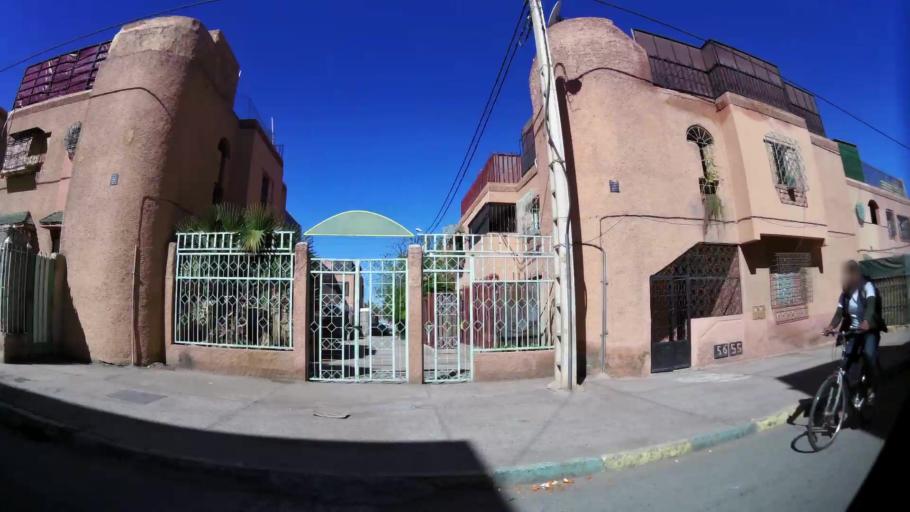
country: MA
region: Marrakech-Tensift-Al Haouz
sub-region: Marrakech
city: Marrakesh
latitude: 31.6462
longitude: -7.9844
